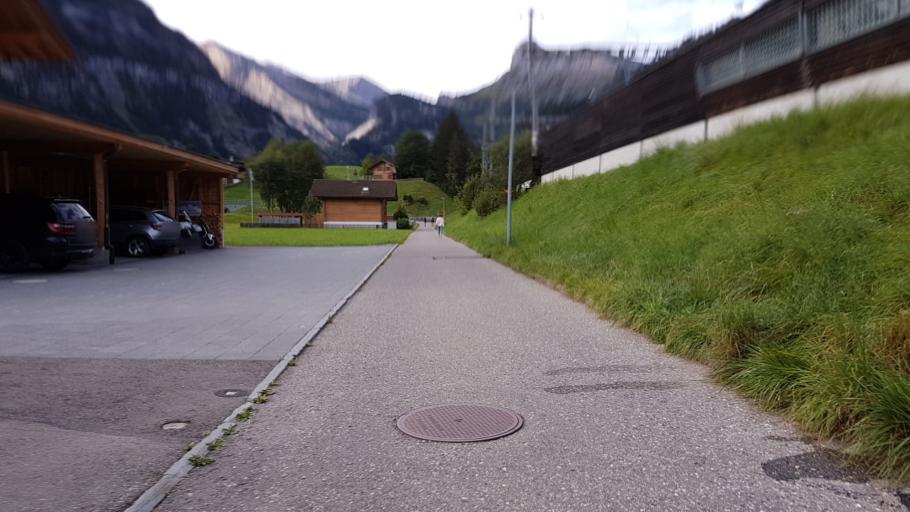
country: CH
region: Bern
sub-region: Frutigen-Niedersimmental District
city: Kandersteg
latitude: 46.4924
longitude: 7.6699
